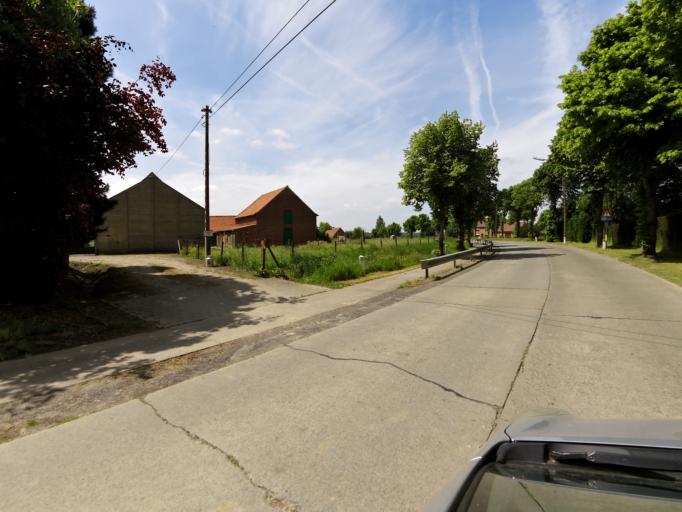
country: BE
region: Flanders
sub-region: Provincie West-Vlaanderen
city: Diksmuide
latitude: 50.9630
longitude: 2.8379
